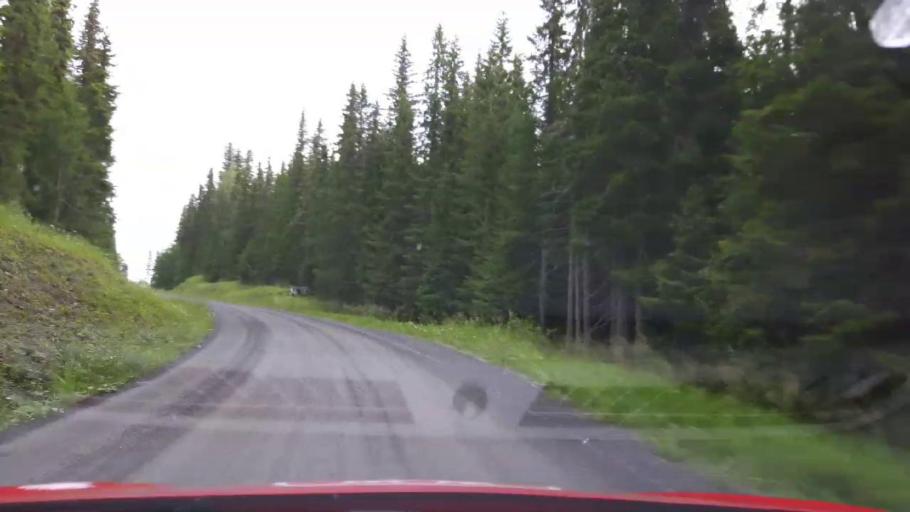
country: SE
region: Jaemtland
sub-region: OEstersunds Kommun
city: Lit
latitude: 63.4341
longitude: 15.2659
